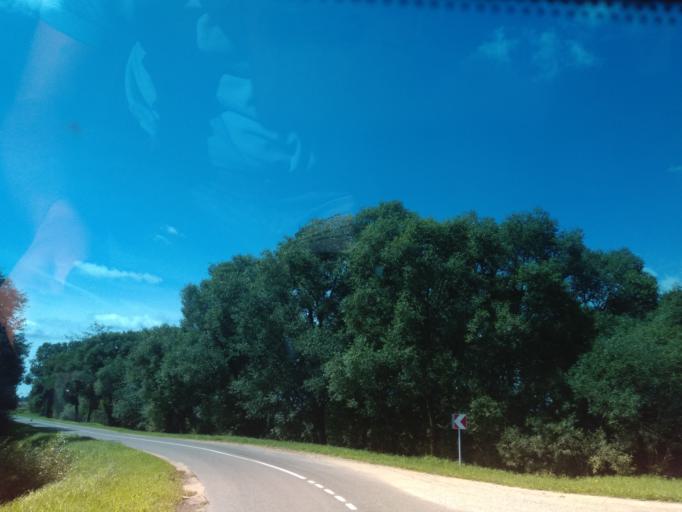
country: BY
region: Minsk
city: Kapyl'
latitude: 53.2735
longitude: 27.2069
